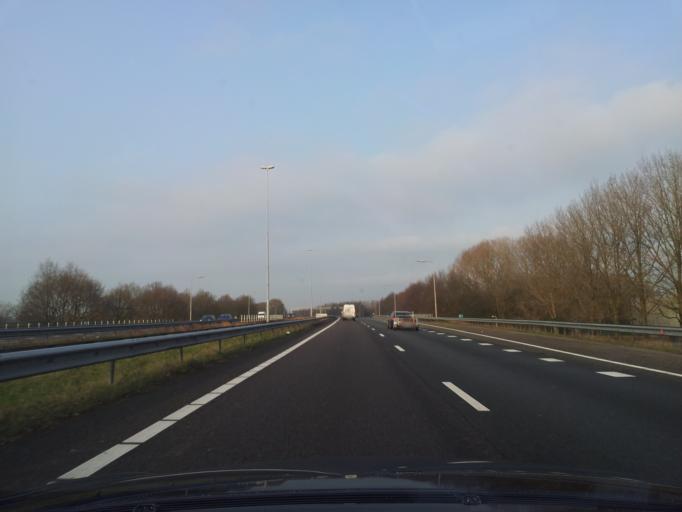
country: NL
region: Utrecht
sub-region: Gemeente Vianen
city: Vianen
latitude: 51.9557
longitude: 5.0396
